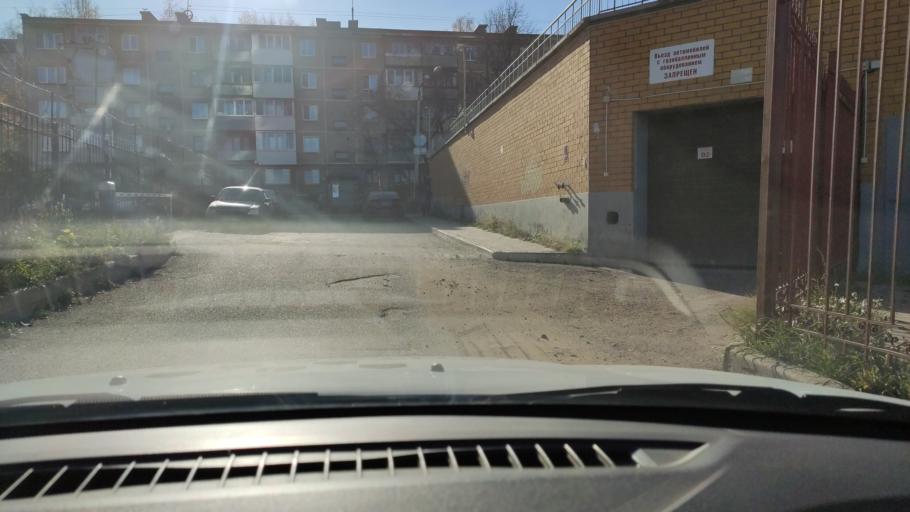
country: RU
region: Perm
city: Perm
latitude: 58.0231
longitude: 56.2697
